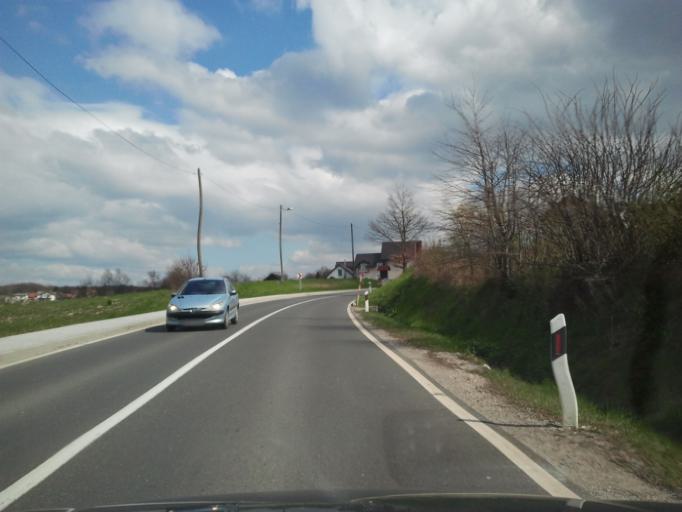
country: HR
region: Grad Zagreb
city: Horvati
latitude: 45.6949
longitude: 15.7490
